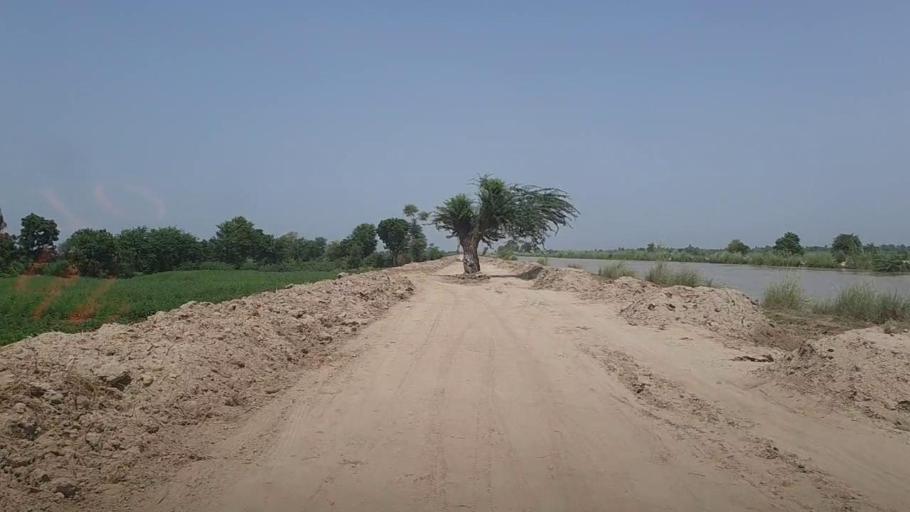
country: PK
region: Sindh
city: Pad Idan
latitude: 26.7956
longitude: 68.2746
